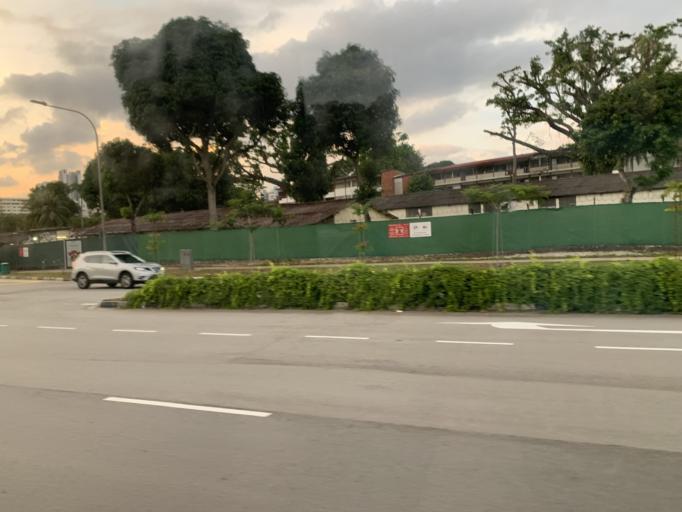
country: SG
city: Singapore
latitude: 1.3194
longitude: 103.7727
